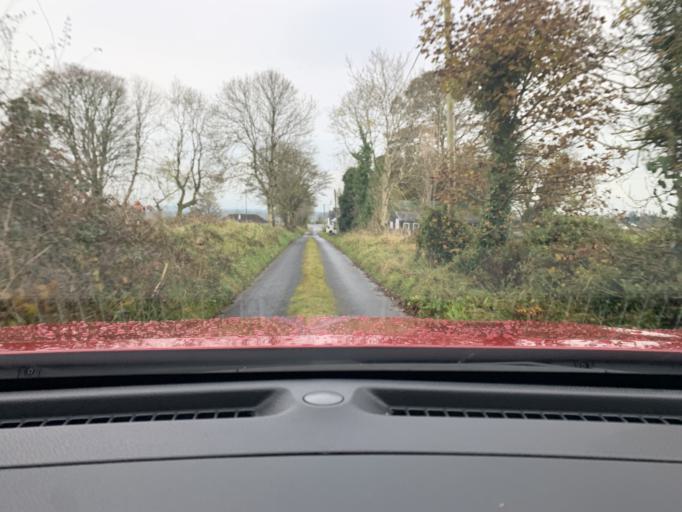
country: IE
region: Connaught
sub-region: Roscommon
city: Ballaghaderreen
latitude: 53.9153
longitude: -8.5549
